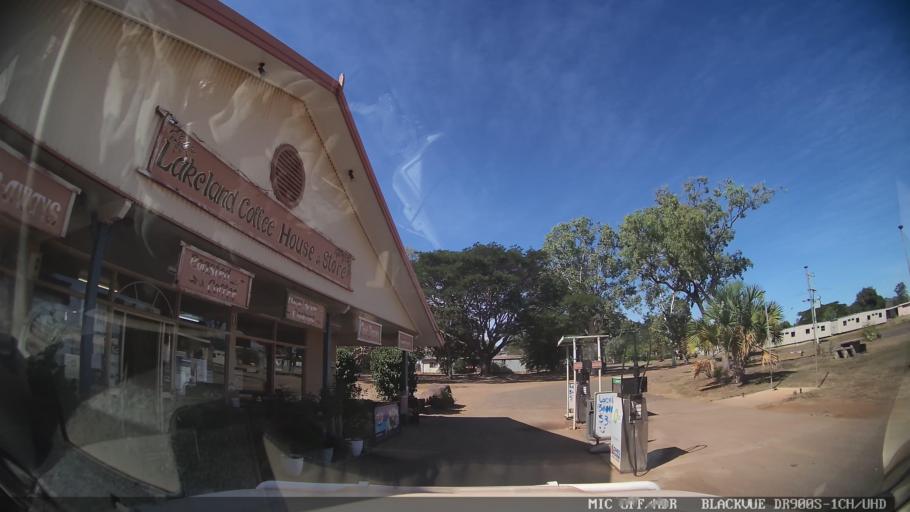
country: AU
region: Queensland
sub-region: Cook
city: Cooktown
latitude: -15.8592
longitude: 144.8551
